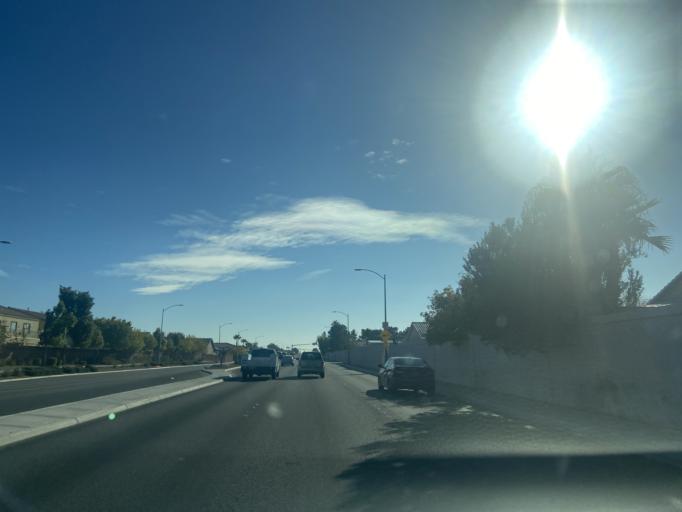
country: US
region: Nevada
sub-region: Clark County
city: North Las Vegas
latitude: 36.2315
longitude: -115.1802
